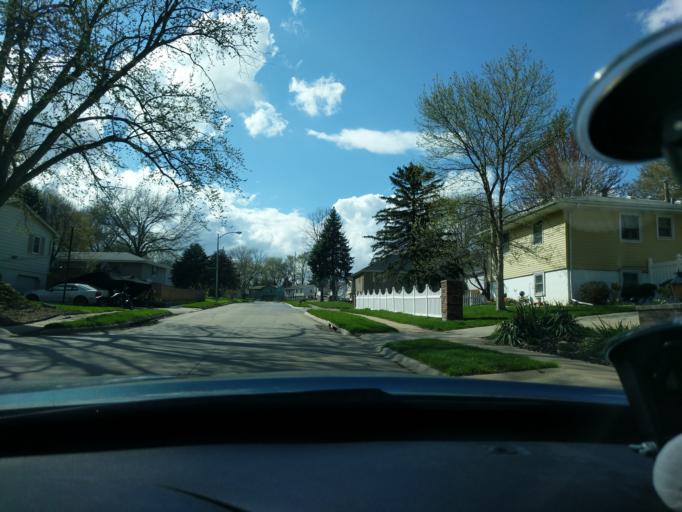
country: US
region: Nebraska
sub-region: Douglas County
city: Ralston
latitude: 41.2329
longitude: -96.0948
